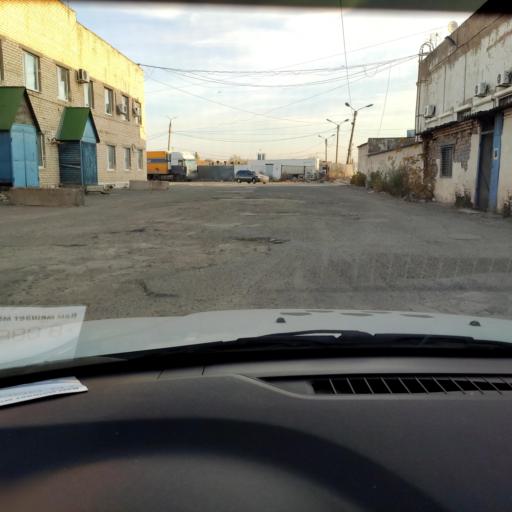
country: RU
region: Samara
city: Zhigulevsk
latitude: 53.5194
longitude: 49.4743
